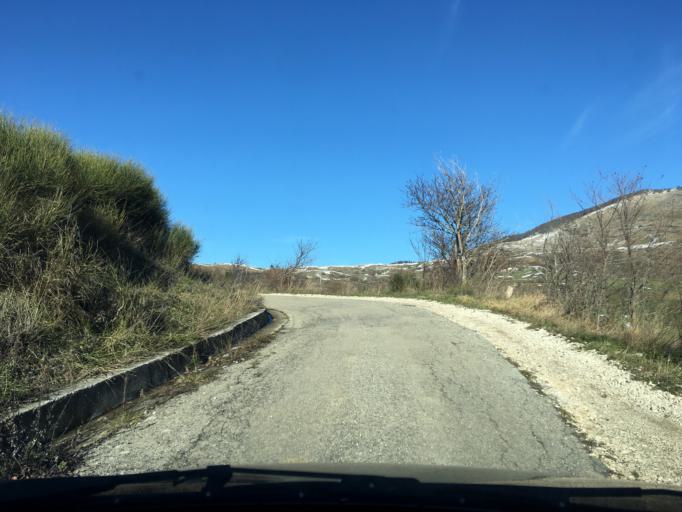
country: IT
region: Molise
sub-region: Provincia di Isernia
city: Agnone
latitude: 41.8425
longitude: 14.3553
